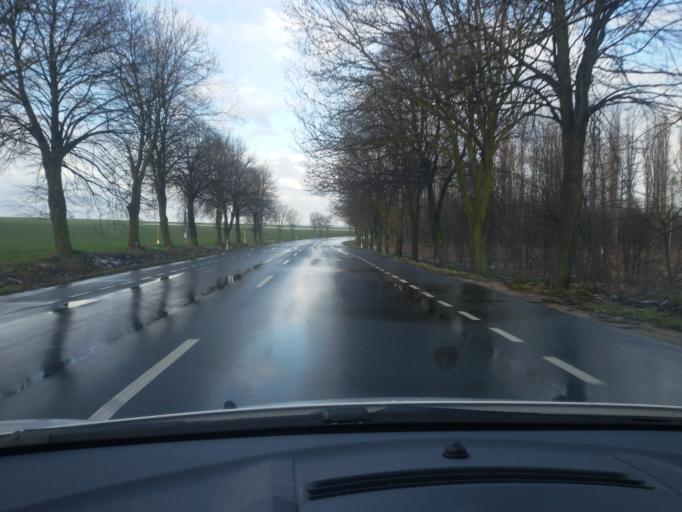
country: PL
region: Lower Silesian Voivodeship
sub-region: Powiat glogowski
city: Glogow
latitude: 51.6668
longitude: 16.0085
